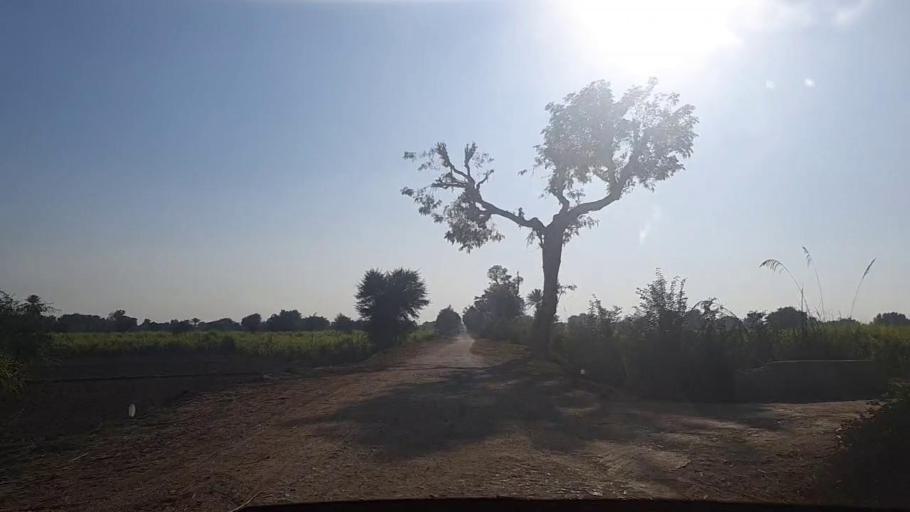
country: PK
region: Sindh
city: Gambat
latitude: 27.3532
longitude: 68.4529
